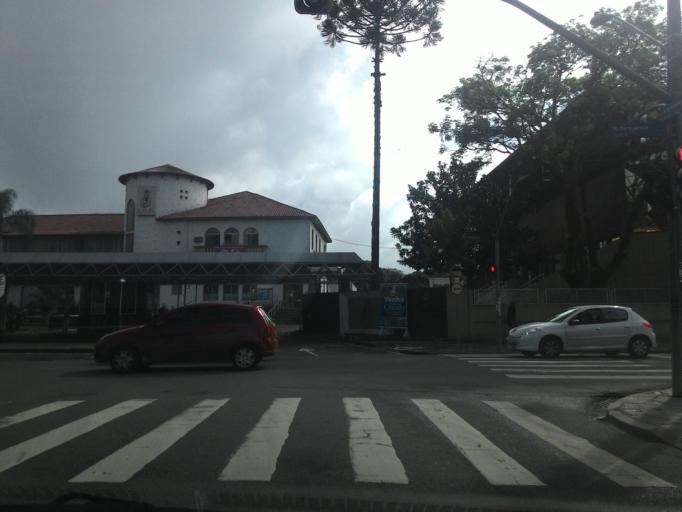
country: BR
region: Parana
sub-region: Curitiba
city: Curitiba
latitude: -25.4265
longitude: -49.2643
